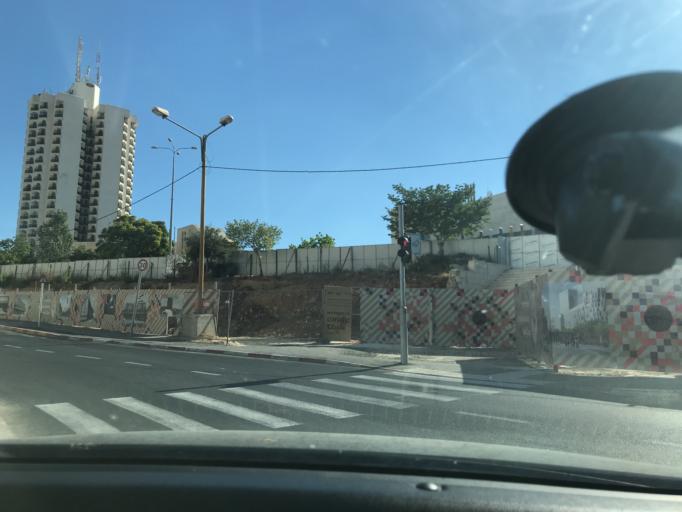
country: IL
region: Jerusalem
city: West Jerusalem
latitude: 31.7867
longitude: 35.2038
